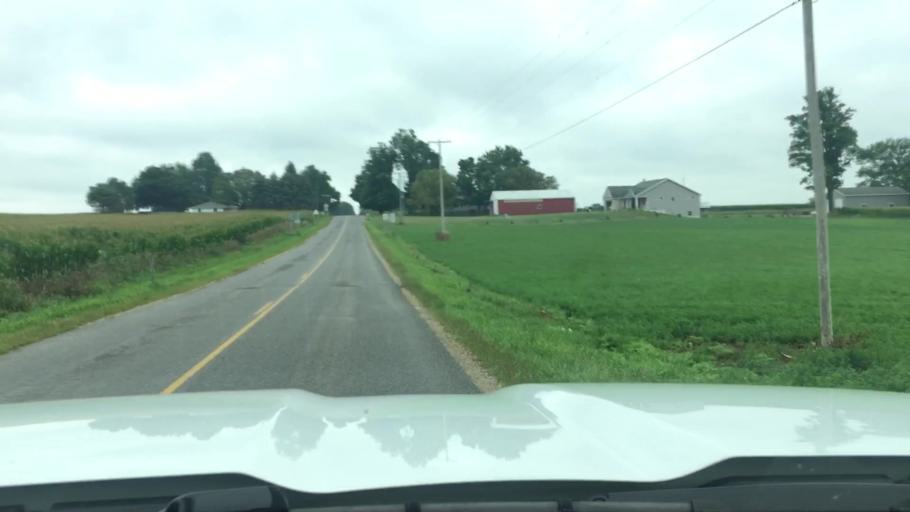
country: US
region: Michigan
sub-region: Ottawa County
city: Hudsonville
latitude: 42.7955
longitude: -85.8617
